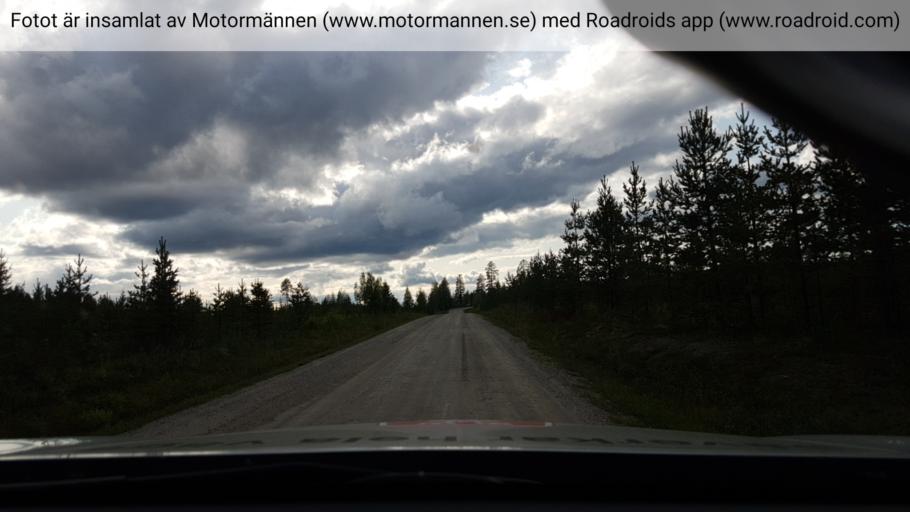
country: SE
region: Vaesterbotten
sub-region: Lycksele Kommun
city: Lycksele
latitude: 64.6766
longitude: 18.7007
